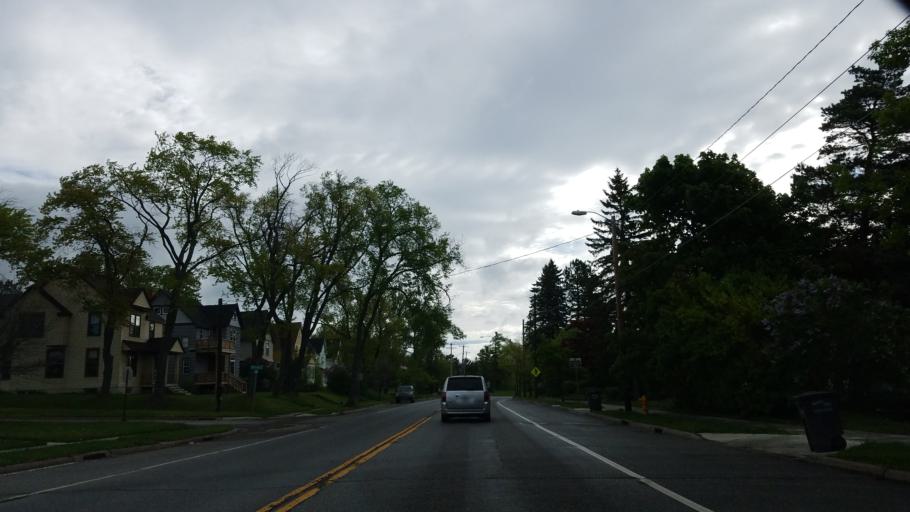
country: US
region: Minnesota
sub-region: Saint Louis County
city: Arnold
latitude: 46.8361
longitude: -92.0102
